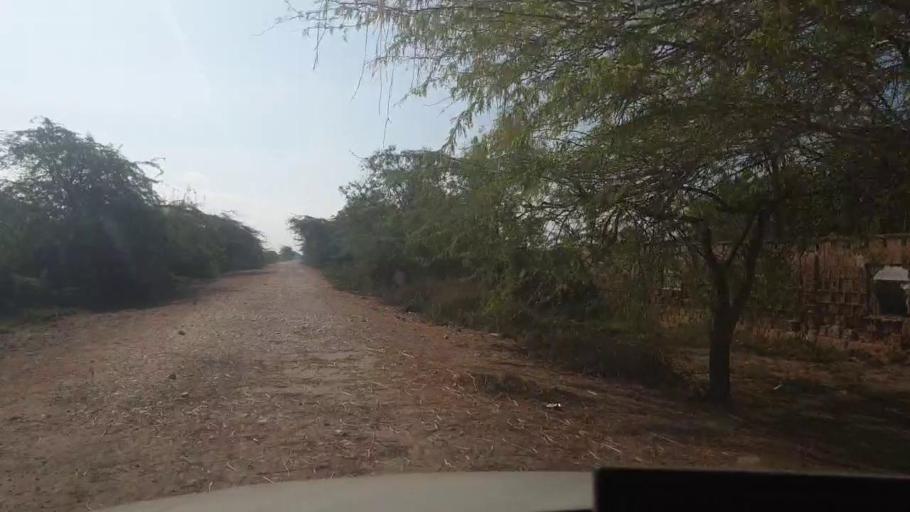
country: PK
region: Sindh
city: Mirpur Sakro
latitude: 24.4733
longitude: 67.5954
